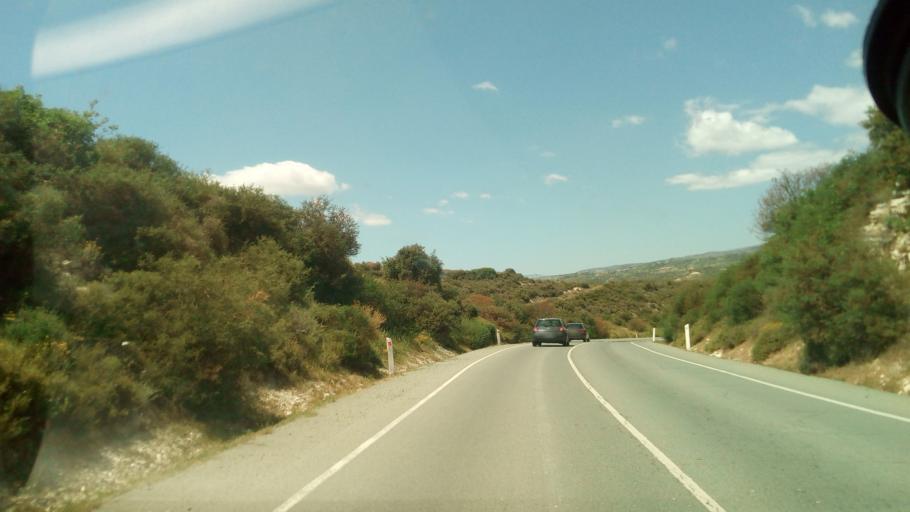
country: CY
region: Limassol
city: Pachna
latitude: 34.7708
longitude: 32.8334
